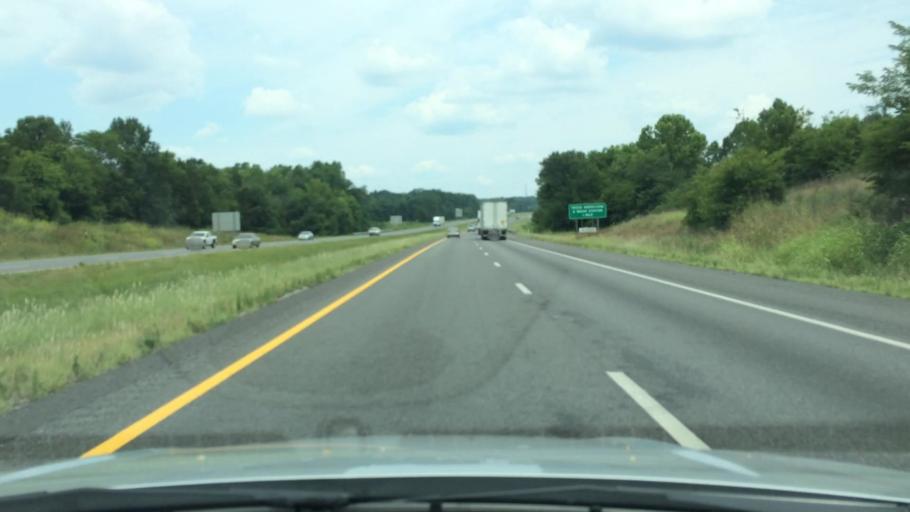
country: US
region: Tennessee
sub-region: Maury County
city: Spring Hill
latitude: 35.6636
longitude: -86.8921
